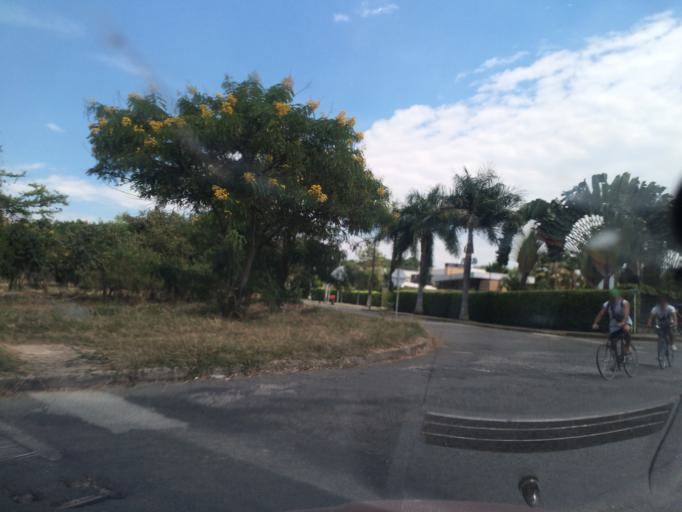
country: CO
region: Valle del Cauca
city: Cali
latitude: 3.3523
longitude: -76.5443
